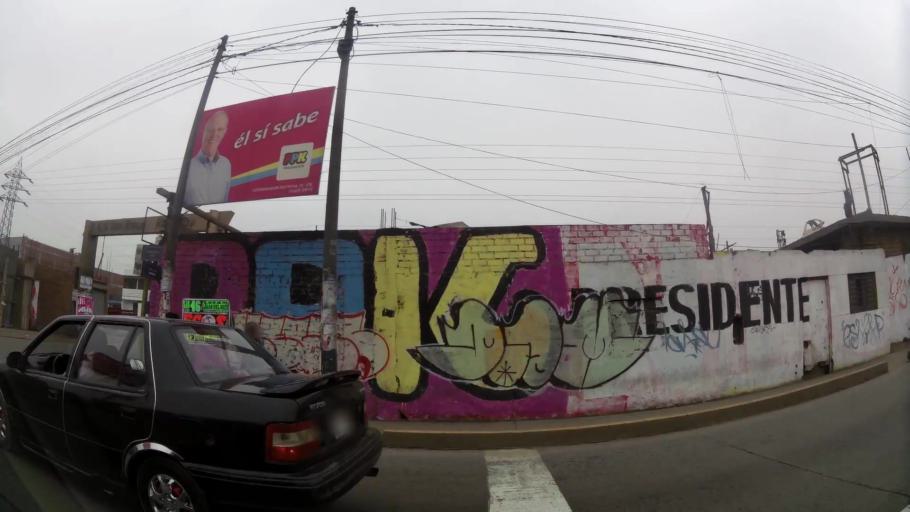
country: PE
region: Lima
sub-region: Lima
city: Santa Maria
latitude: -12.0224
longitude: -76.9090
